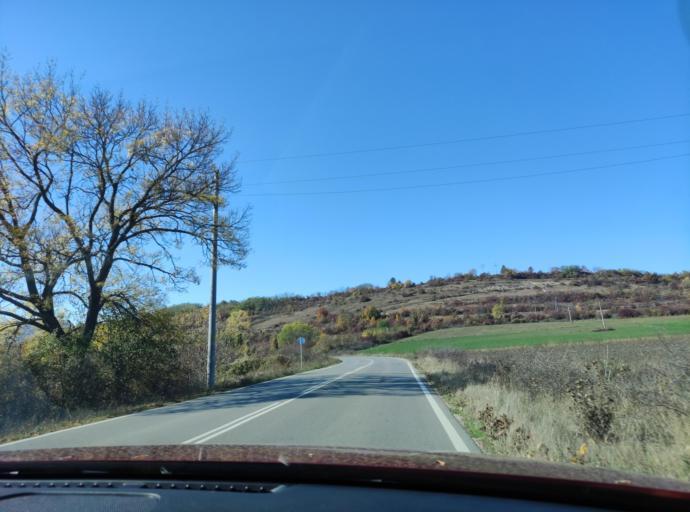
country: BG
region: Montana
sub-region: Obshtina Montana
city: Montana
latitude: 43.4011
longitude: 23.1327
